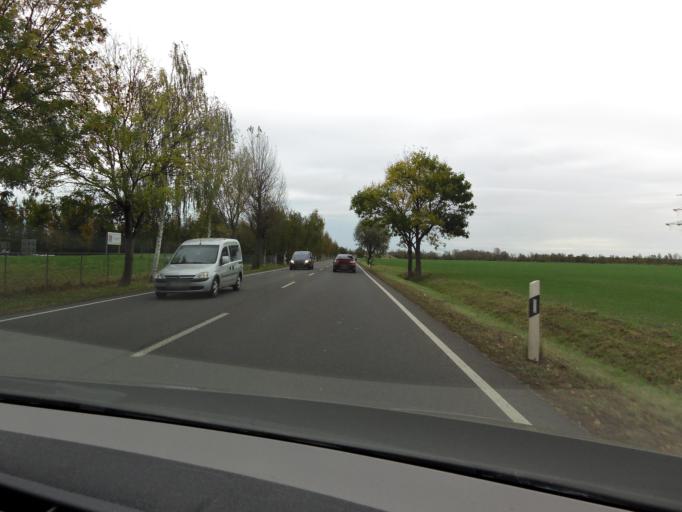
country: DE
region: Saxony
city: Zwenkau
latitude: 51.2084
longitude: 12.3381
